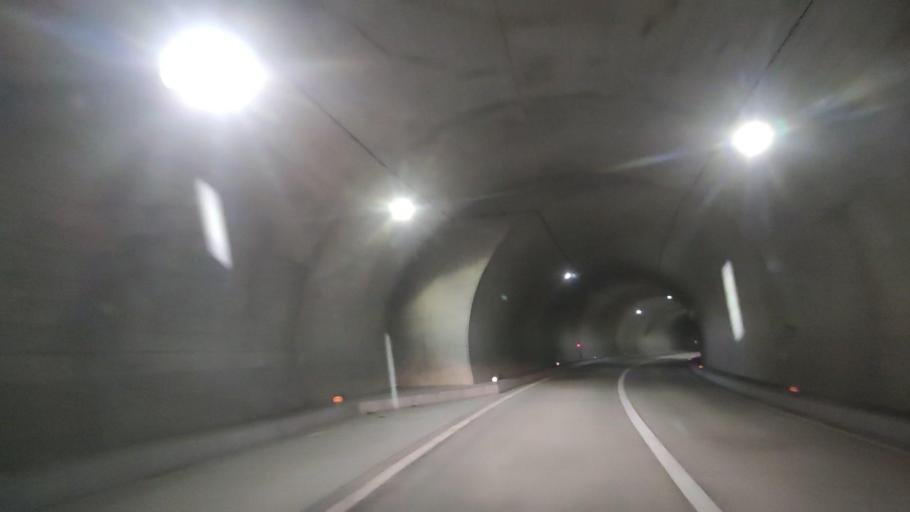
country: JP
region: Tottori
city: Tottori
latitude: 35.3499
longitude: 134.4718
